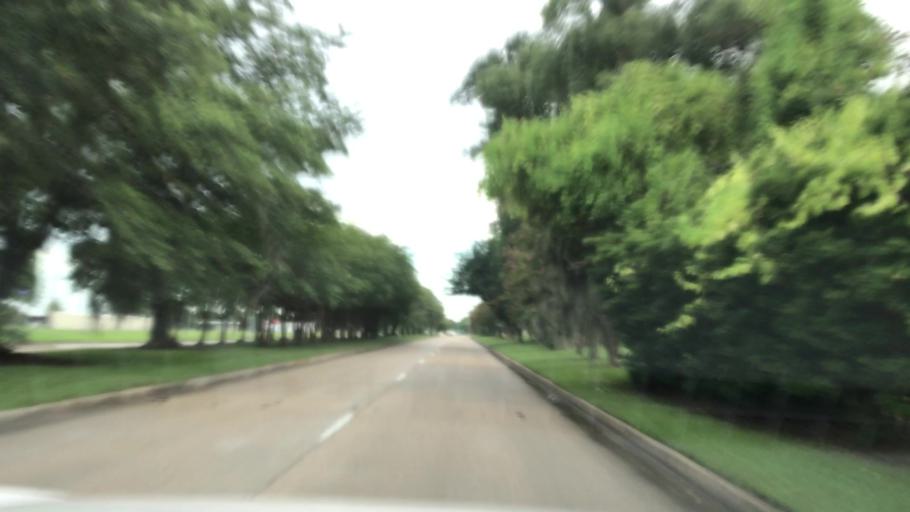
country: US
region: Louisiana
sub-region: East Baton Rouge Parish
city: Brownsfield
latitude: 30.5288
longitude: -91.1613
